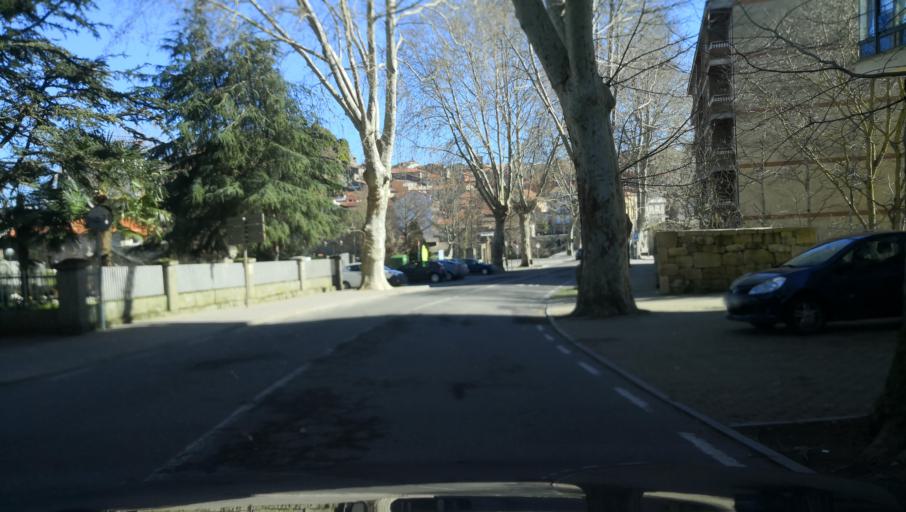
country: ES
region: Galicia
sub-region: Provincia de Ourense
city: Allariz
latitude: 42.1900
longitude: -7.8059
